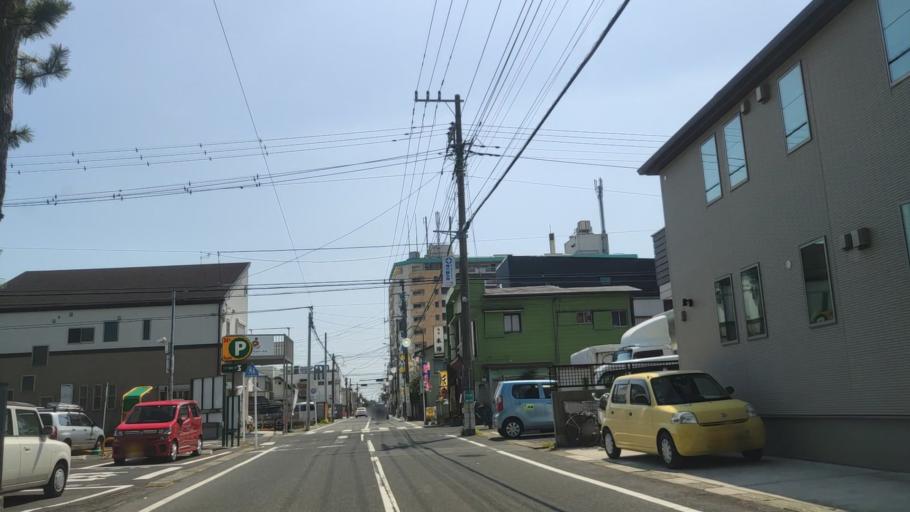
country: JP
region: Kanagawa
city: Hiratsuka
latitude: 35.3197
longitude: 139.3390
